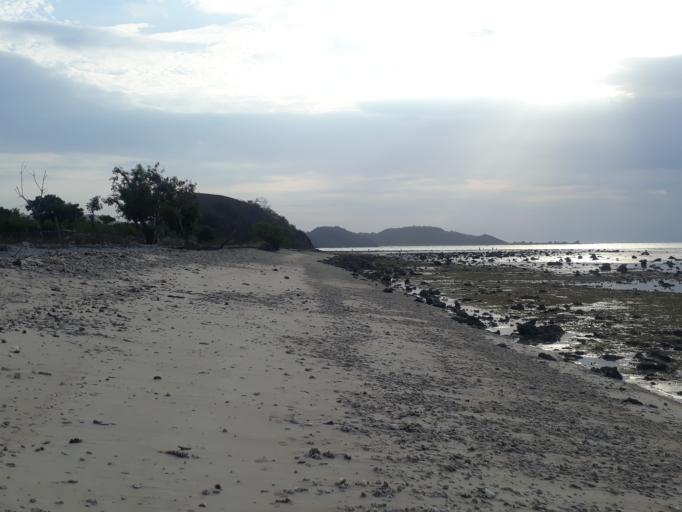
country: ID
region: West Nusa Tenggara
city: Tawun
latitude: -8.7318
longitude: 115.8880
